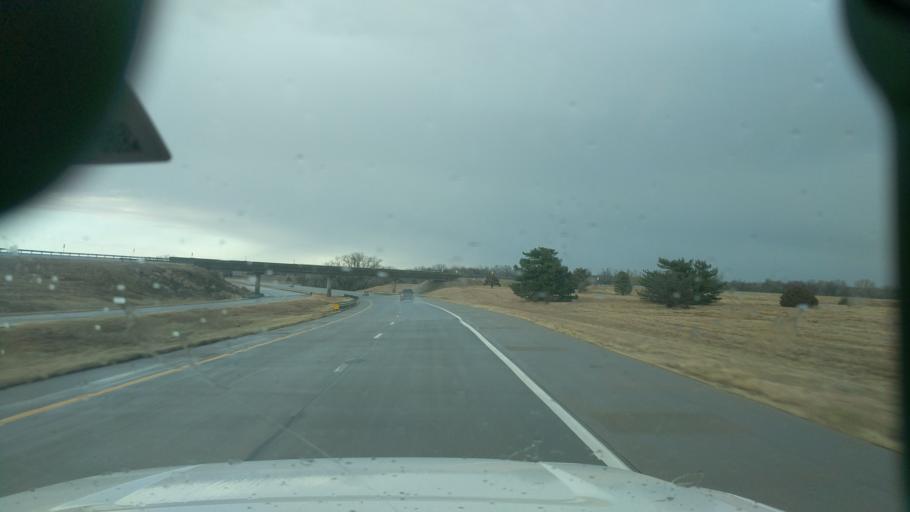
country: US
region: Kansas
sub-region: Harvey County
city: North Newton
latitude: 38.0636
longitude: -97.3225
